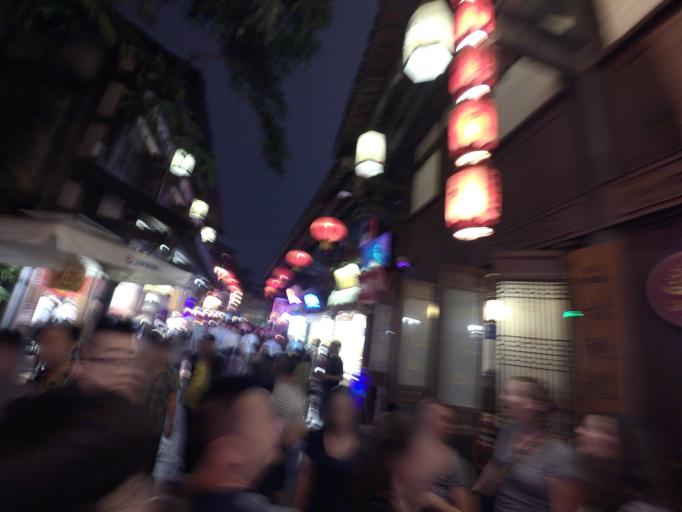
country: CN
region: Sichuan
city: Chengdu
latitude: 30.6491
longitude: 104.0474
